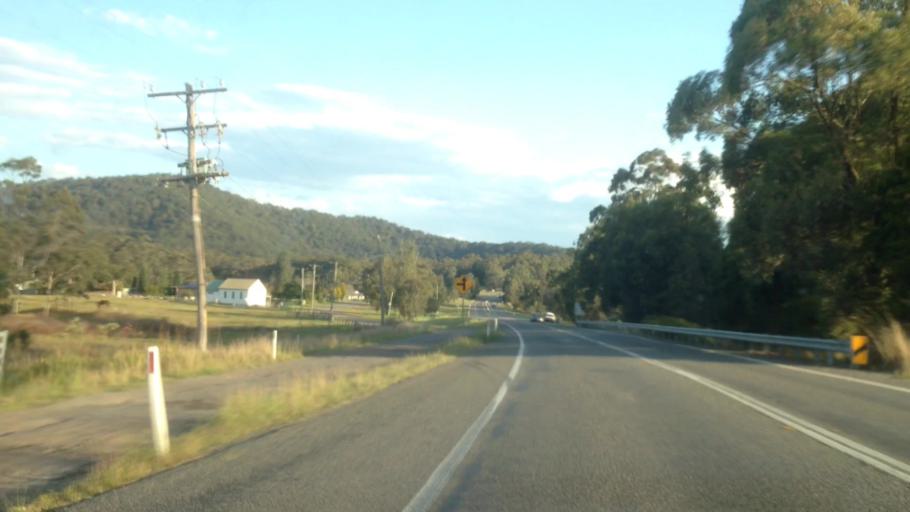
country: AU
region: New South Wales
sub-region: Lake Macquarie Shire
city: Holmesville
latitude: -32.9499
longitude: 151.4791
